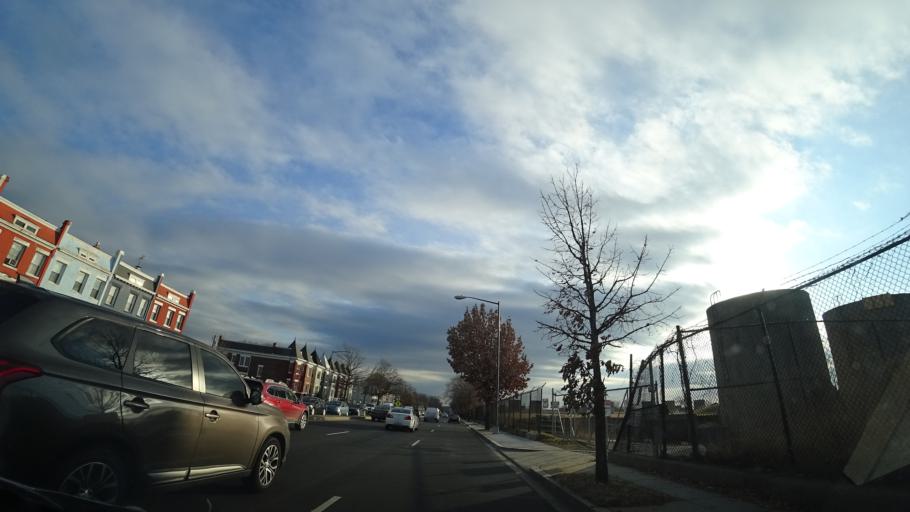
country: US
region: Washington, D.C.
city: Washington, D.C.
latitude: 38.9257
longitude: -77.0092
